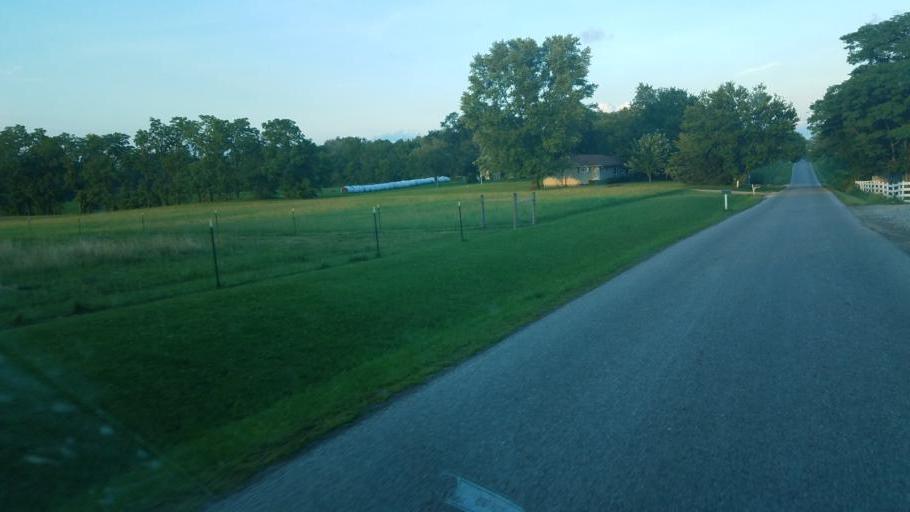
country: US
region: Ohio
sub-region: Knox County
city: Fredericktown
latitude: 40.5352
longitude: -82.6535
